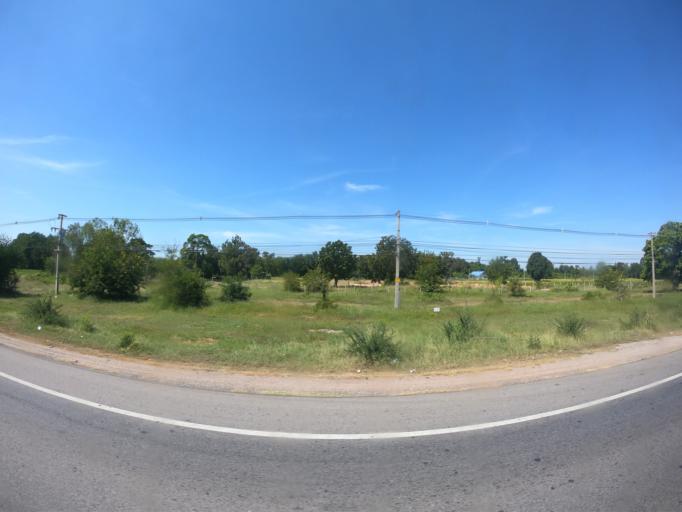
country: TH
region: Khon Kaen
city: Phon
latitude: 15.8380
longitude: 102.6105
